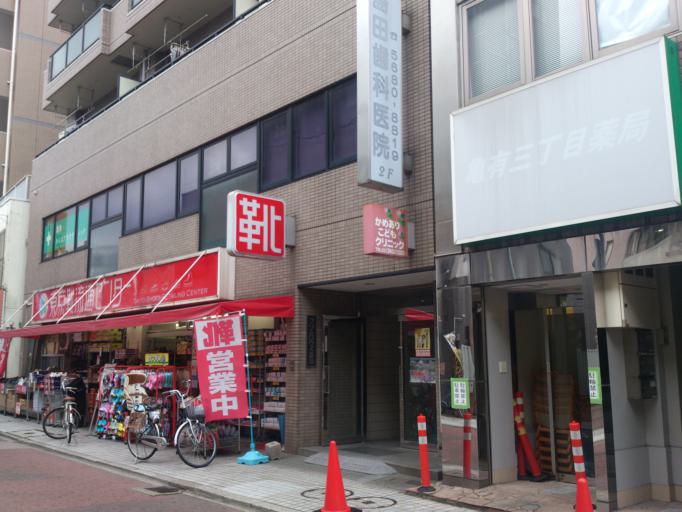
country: JP
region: Chiba
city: Matsudo
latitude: 35.7634
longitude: 139.8490
